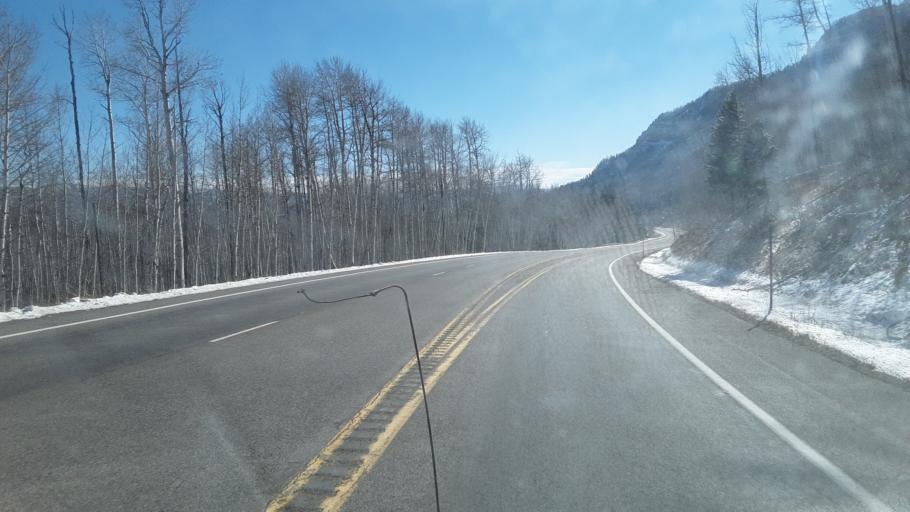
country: US
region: Colorado
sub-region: La Plata County
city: Durango
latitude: 37.5623
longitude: -107.8233
